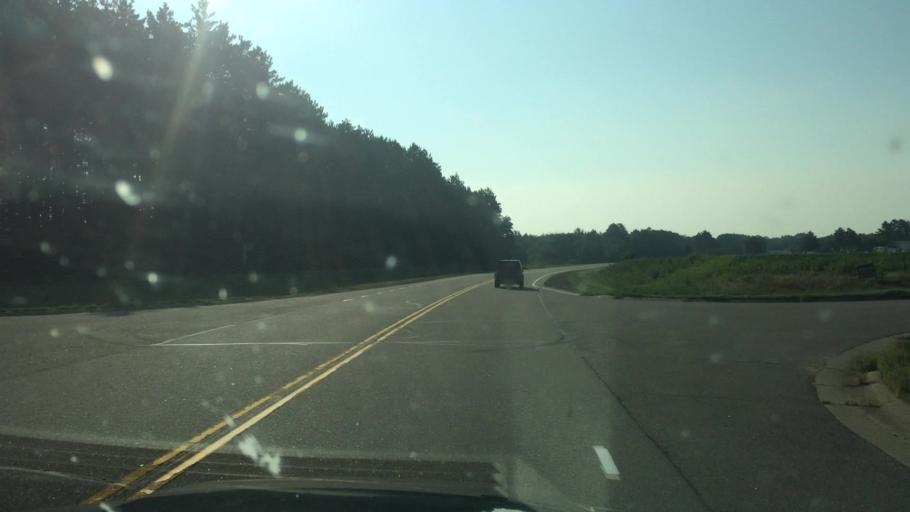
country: US
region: Wisconsin
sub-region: Langlade County
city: Antigo
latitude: 45.1471
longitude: -89.2502
